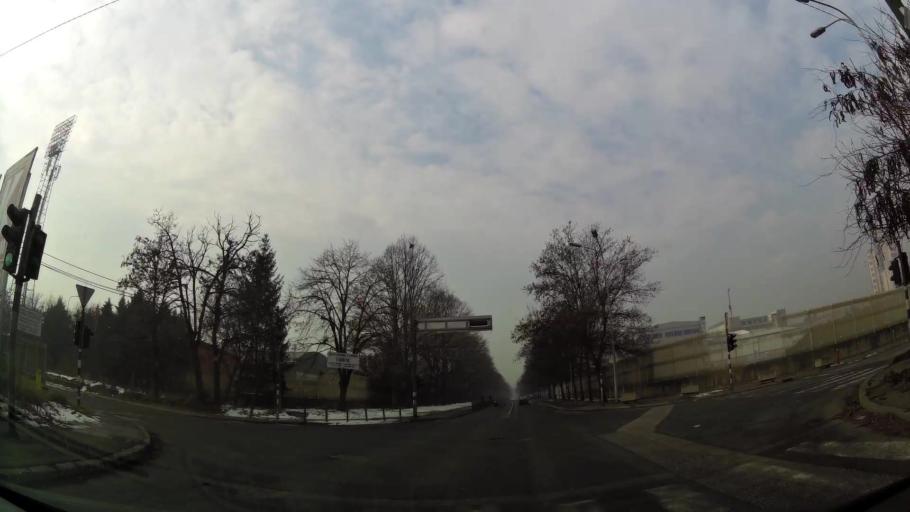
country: MK
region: Cair
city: Cair
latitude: 41.9996
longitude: 21.4691
